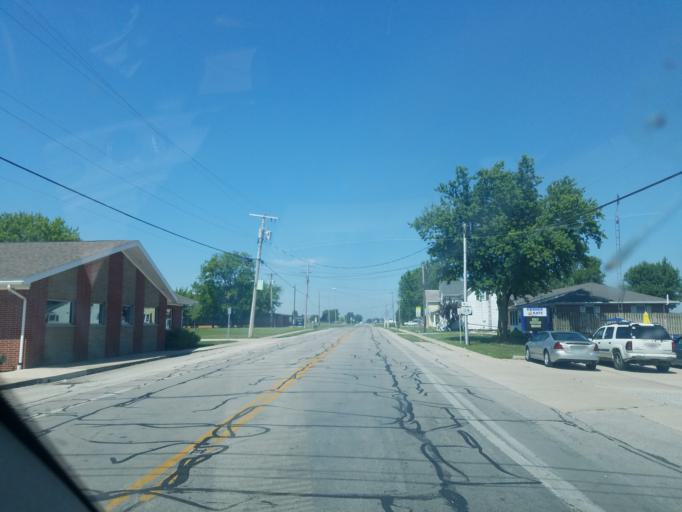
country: US
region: Ohio
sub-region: Auglaize County
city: New Bremen
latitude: 40.4076
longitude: -84.4937
